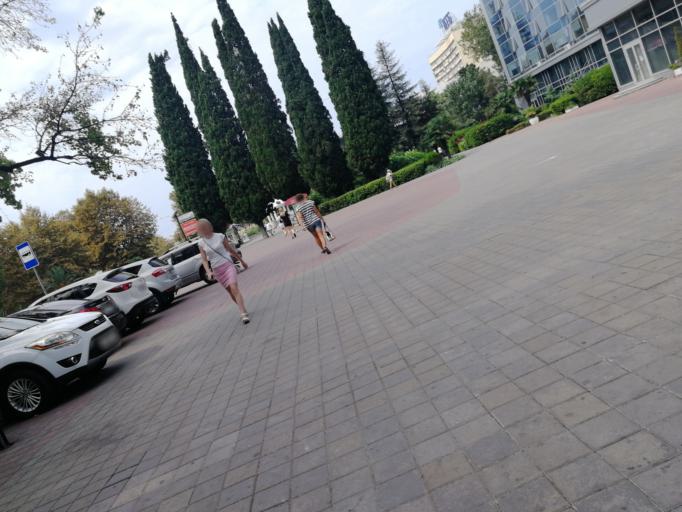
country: RU
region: Krasnodarskiy
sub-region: Sochi City
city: Sochi
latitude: 43.5831
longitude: 39.7219
